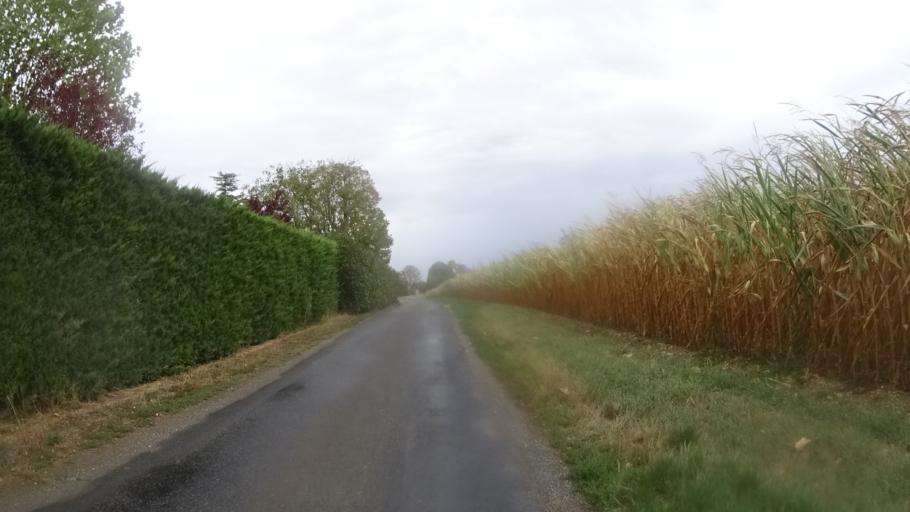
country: FR
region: Centre
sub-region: Departement du Loiret
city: Boynes
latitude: 48.1821
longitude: 2.3783
